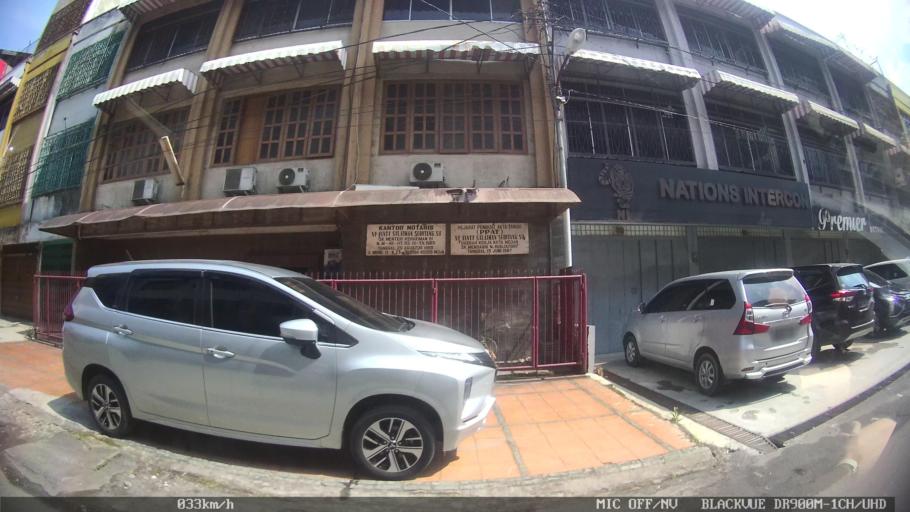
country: ID
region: North Sumatra
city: Medan
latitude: 3.5910
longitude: 98.6642
